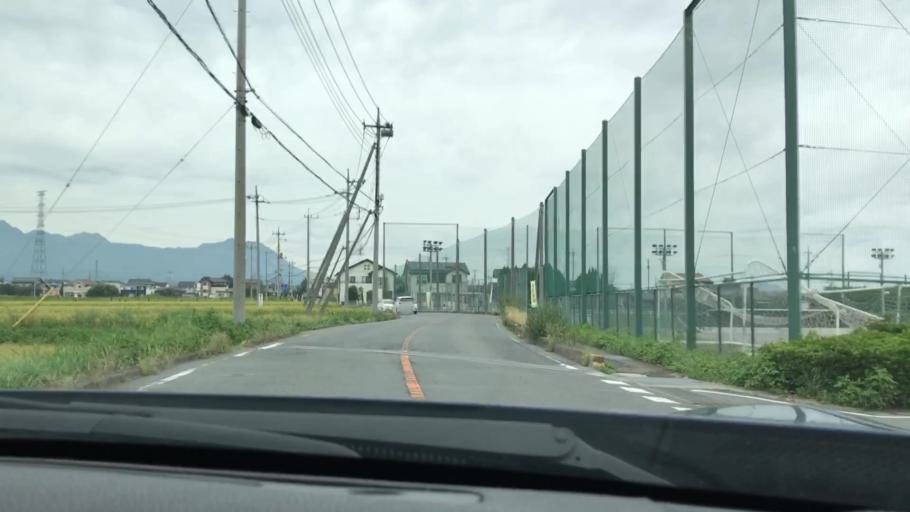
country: JP
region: Gunma
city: Kanekomachi
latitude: 36.4005
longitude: 138.9898
